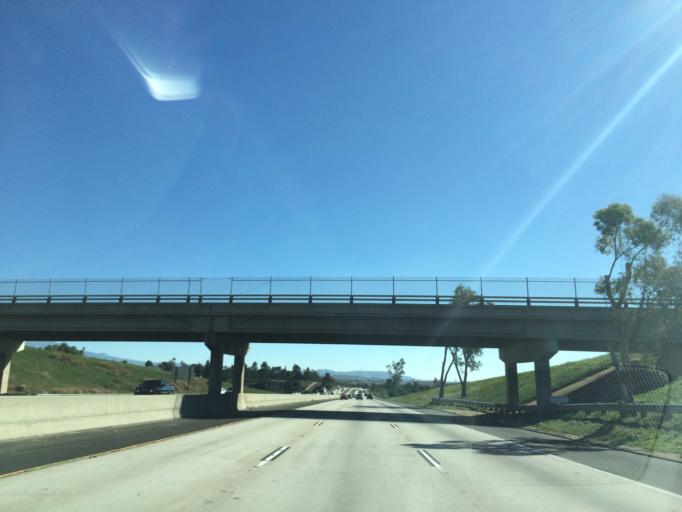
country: US
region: California
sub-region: Riverside County
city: Calimesa
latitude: 33.9936
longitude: -117.0589
